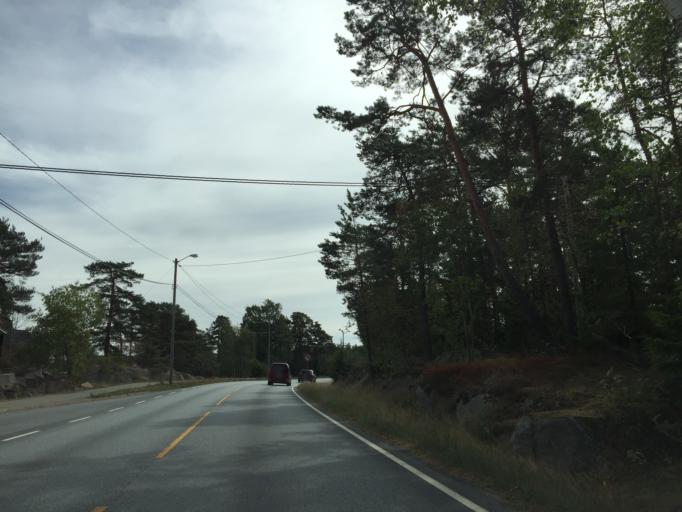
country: NO
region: Ostfold
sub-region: Fredrikstad
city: Fredrikstad
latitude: 59.1154
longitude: 10.9103
